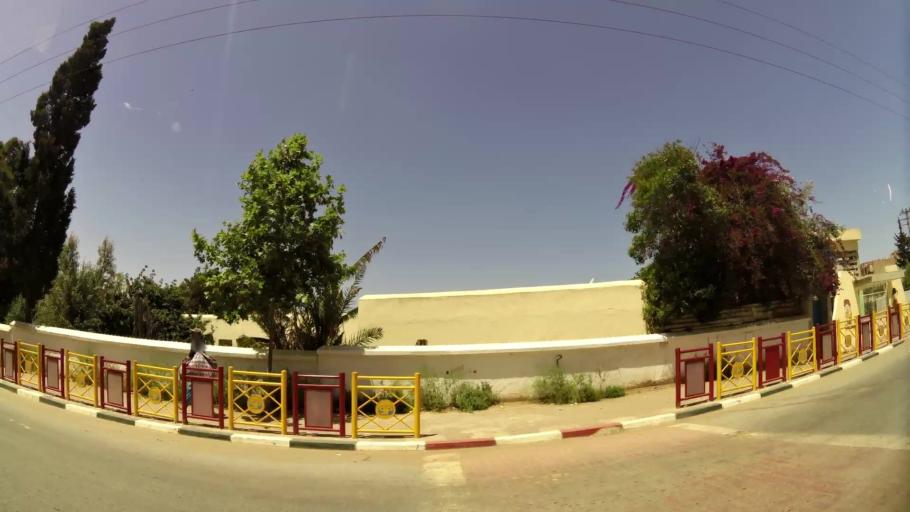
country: MA
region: Rabat-Sale-Zemmour-Zaer
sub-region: Khemisset
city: Khemisset
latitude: 33.8301
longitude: -6.0778
